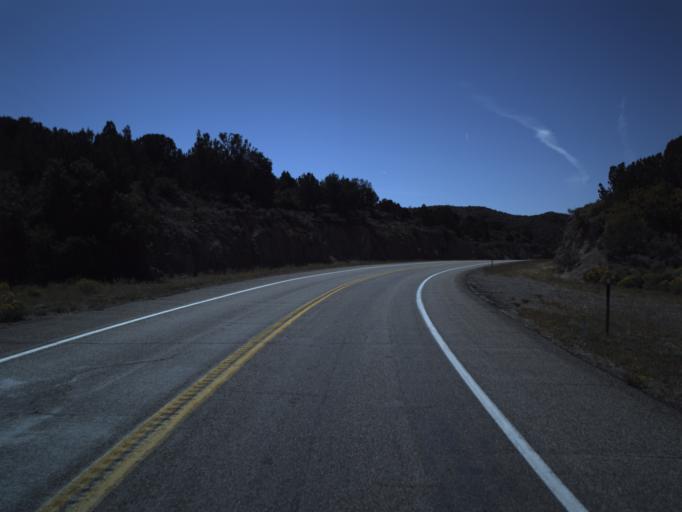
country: US
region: Utah
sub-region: Washington County
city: Enterprise
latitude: 37.4739
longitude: -113.6277
